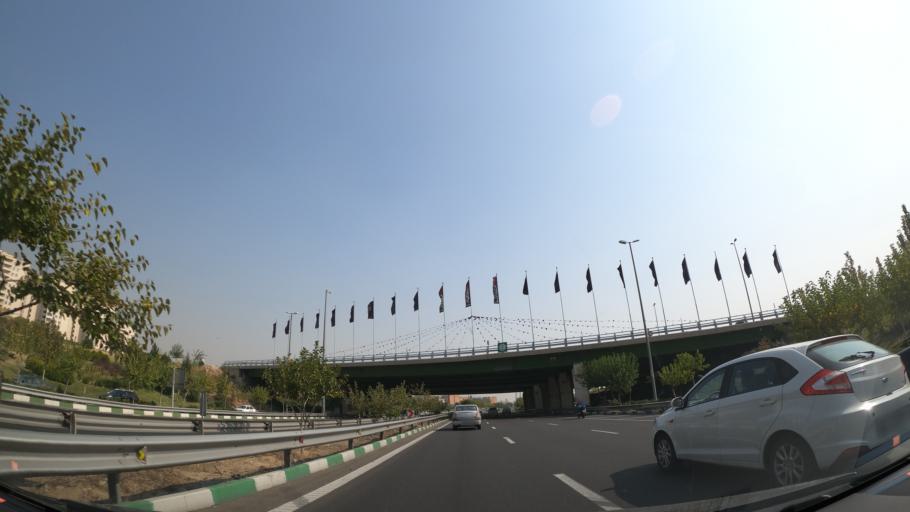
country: IR
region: Tehran
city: Shahr-e Qods
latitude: 35.7600
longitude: 51.2543
